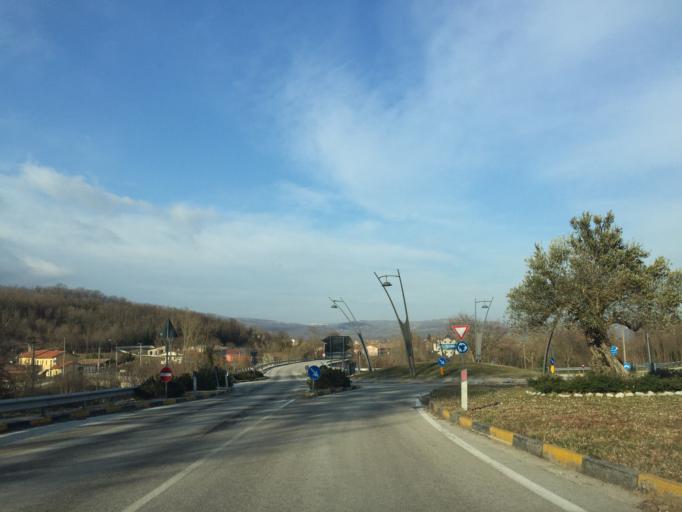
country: IT
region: Molise
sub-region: Provincia di Campobasso
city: San Massimo
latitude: 41.4990
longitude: 14.4134
